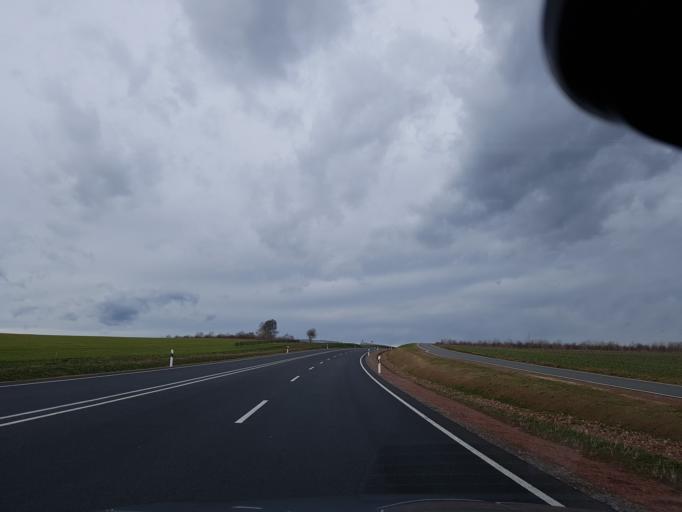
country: DE
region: Saxony
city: Rossau
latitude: 51.0331
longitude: 13.1113
